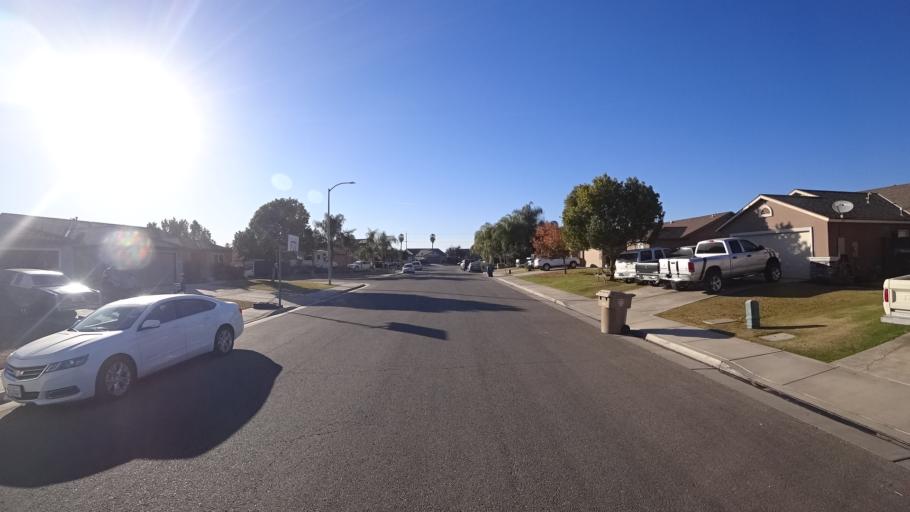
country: US
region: California
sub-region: Kern County
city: Greenfield
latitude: 35.2785
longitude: -119.0002
